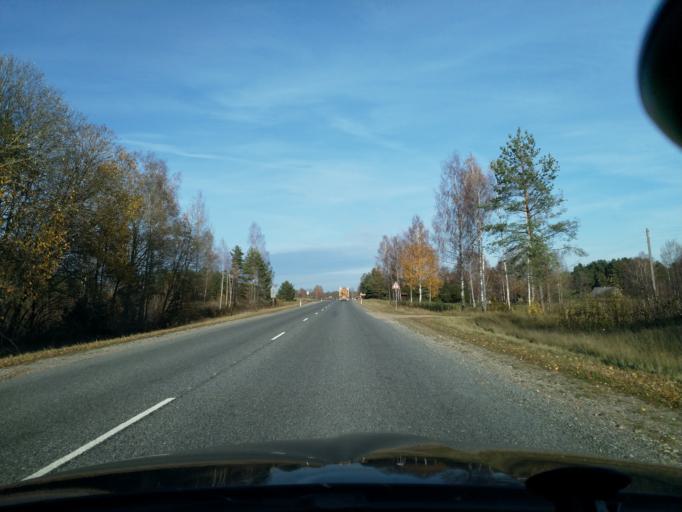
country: LV
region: Kuldigas Rajons
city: Kuldiga
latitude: 56.9547
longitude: 21.9421
